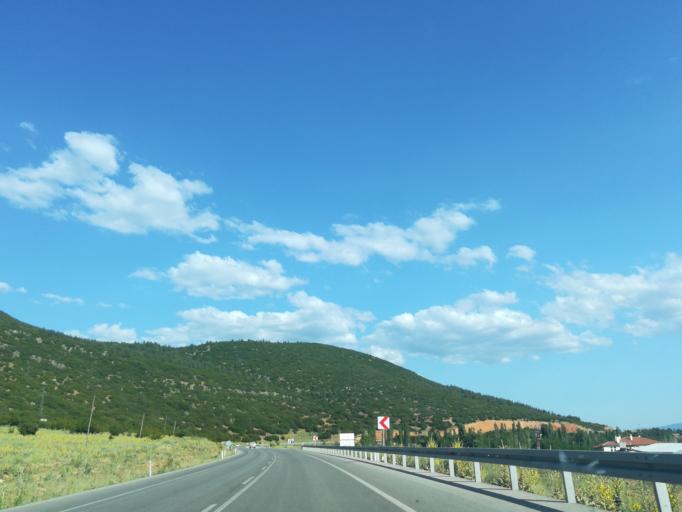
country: TR
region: Denizli
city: Ishakli
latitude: 38.1623
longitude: 30.0789
